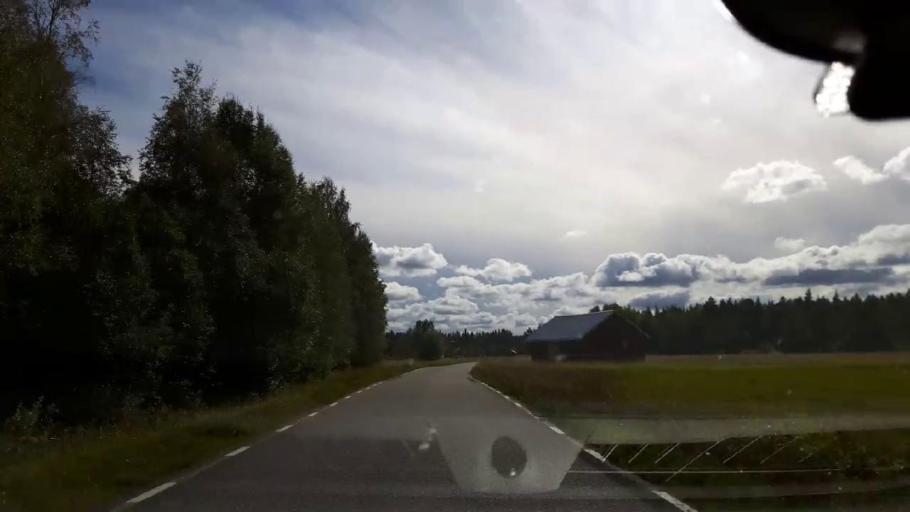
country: SE
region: Jaemtland
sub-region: Braecke Kommun
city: Braecke
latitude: 63.2100
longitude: 15.3499
